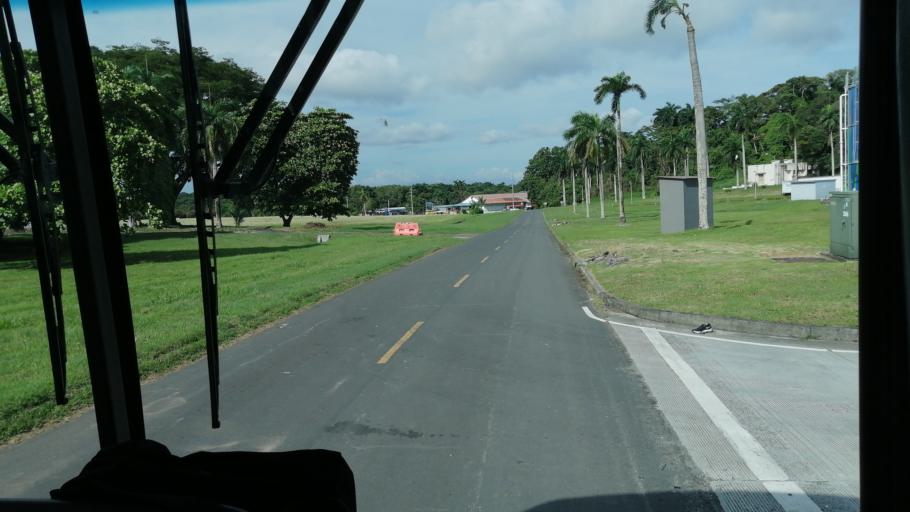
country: PA
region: Panama
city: Veracruz
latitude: 8.9183
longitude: -79.5935
